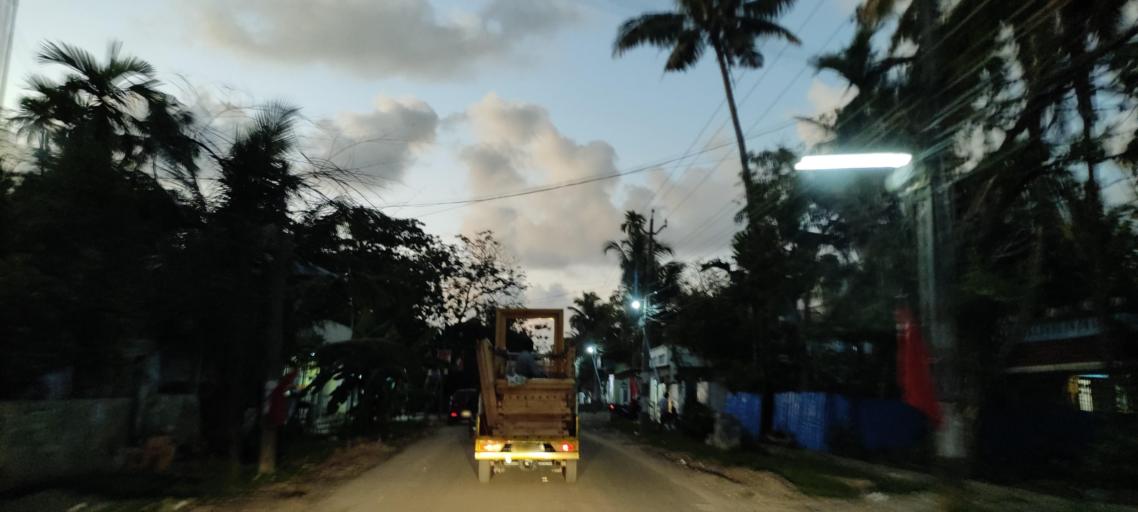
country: IN
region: Kerala
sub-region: Alappuzha
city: Kutiatodu
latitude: 9.8073
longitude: 76.2764
